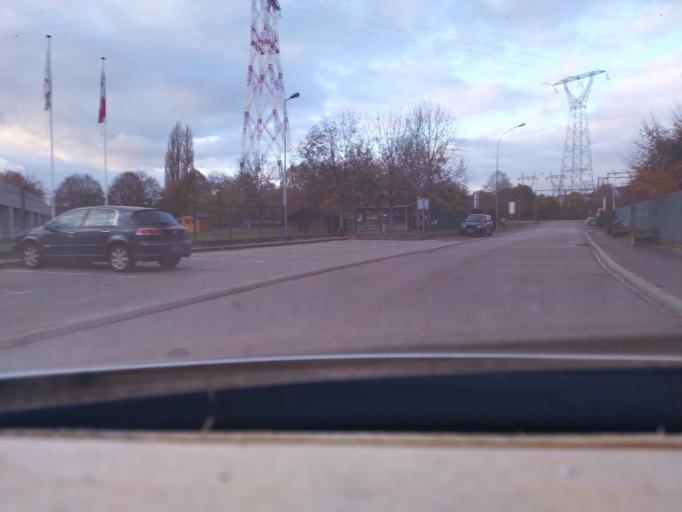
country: FR
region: Haute-Normandie
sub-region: Departement de la Seine-Maritime
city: Yainville
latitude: 49.4572
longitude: 0.8224
